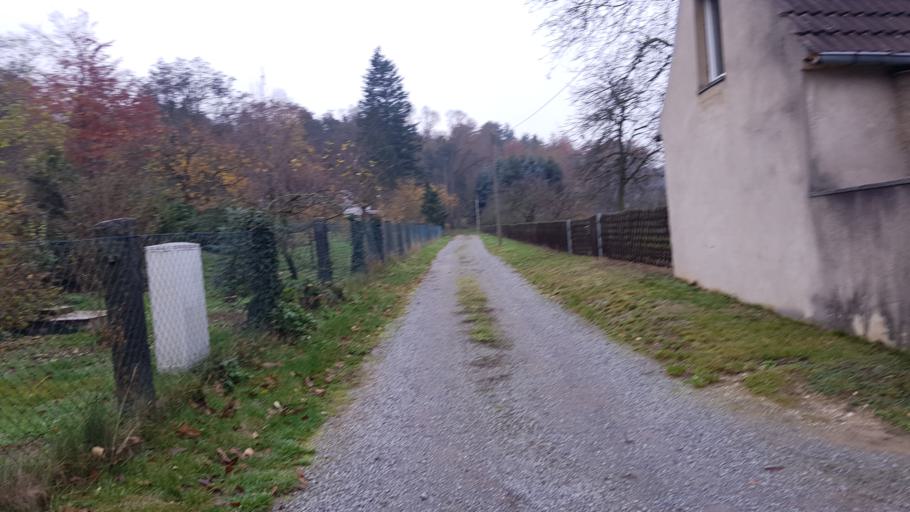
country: DE
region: Brandenburg
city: Grosskmehlen
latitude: 51.3740
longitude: 13.7332
